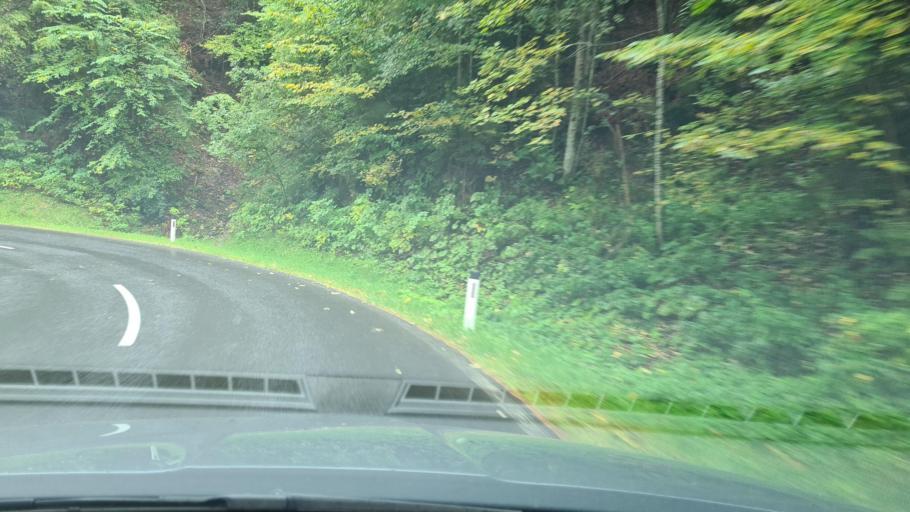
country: AT
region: Styria
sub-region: Politischer Bezirk Weiz
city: Gasen
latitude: 47.3677
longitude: 15.4777
